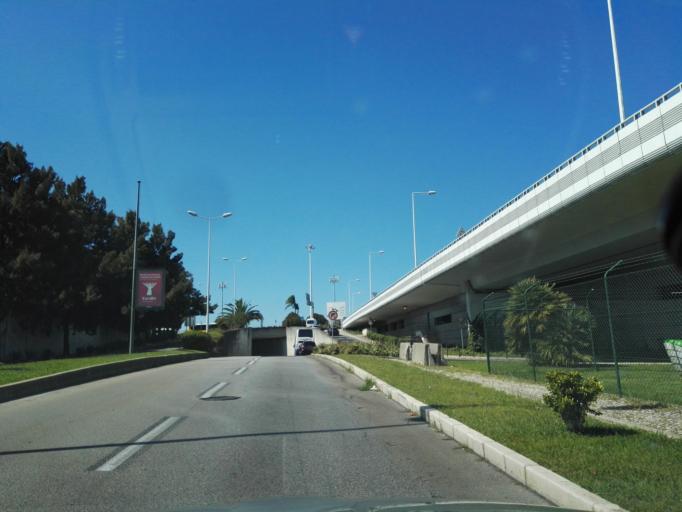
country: PT
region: Lisbon
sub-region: Loures
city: Moscavide
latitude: 38.7672
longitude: -9.1273
